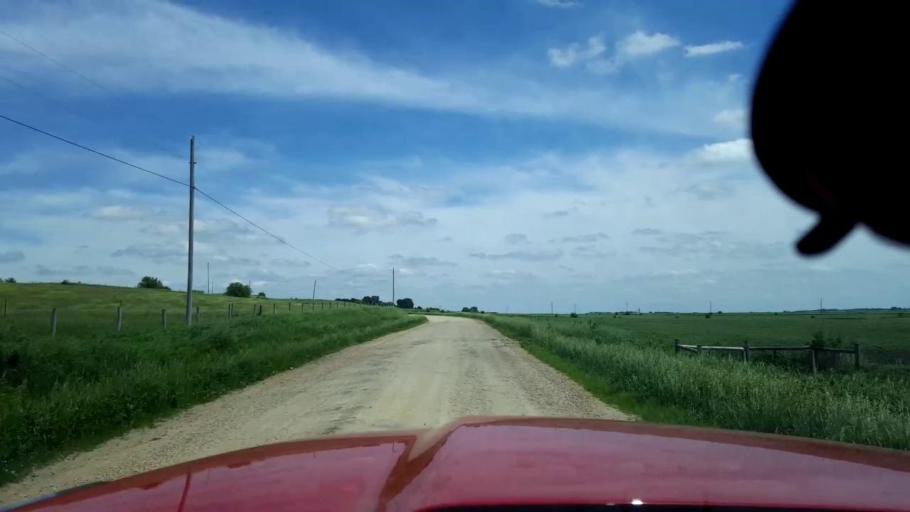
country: US
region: Iowa
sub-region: Linn County
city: Lisbon
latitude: 41.9517
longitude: -91.3541
